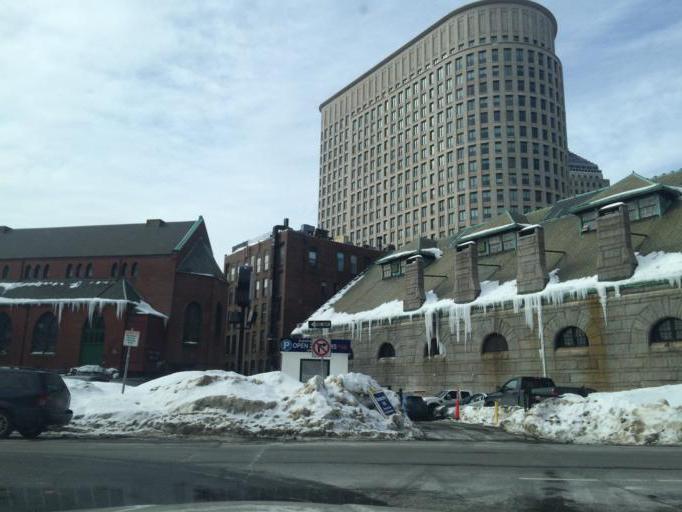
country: US
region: Massachusetts
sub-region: Suffolk County
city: Boston
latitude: 42.3494
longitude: -71.0694
